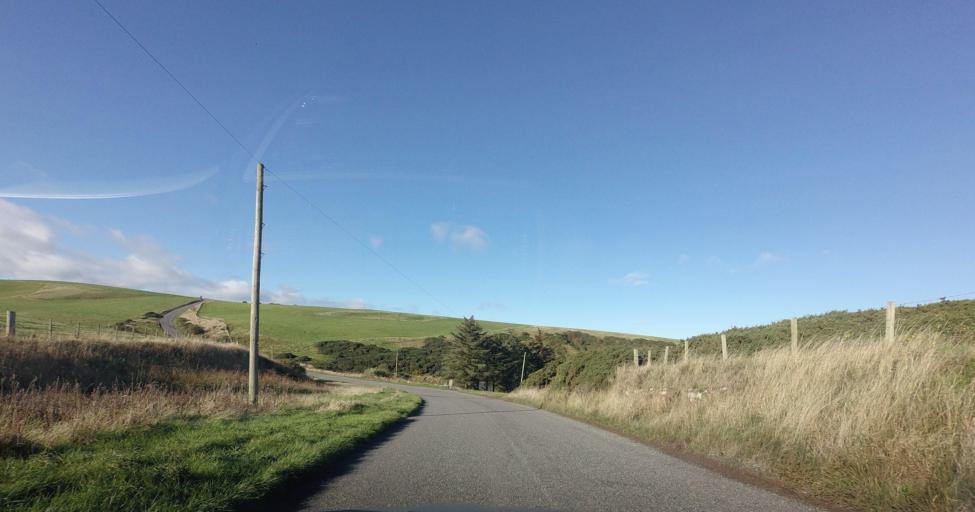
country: GB
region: Scotland
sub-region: Aberdeenshire
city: Rosehearty
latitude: 57.6800
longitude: -2.2694
